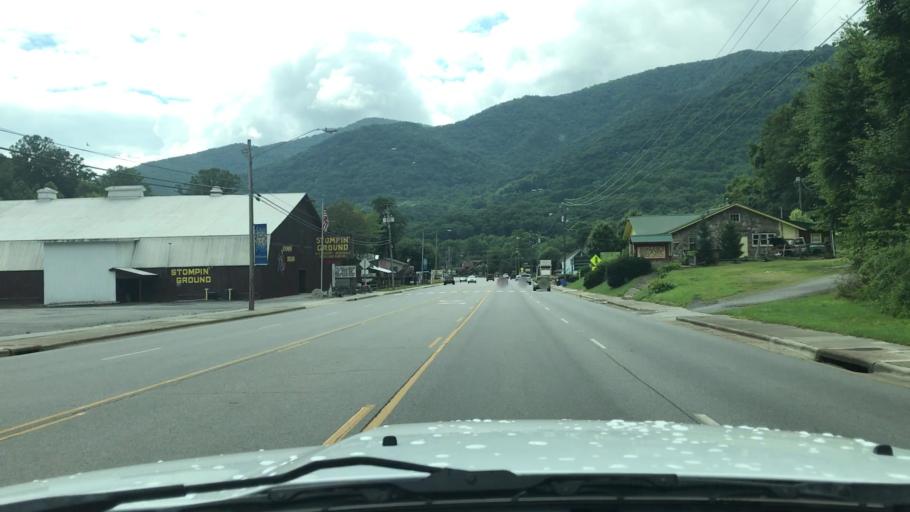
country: US
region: North Carolina
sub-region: Haywood County
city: Maggie Valley
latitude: 35.5141
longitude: -83.0816
